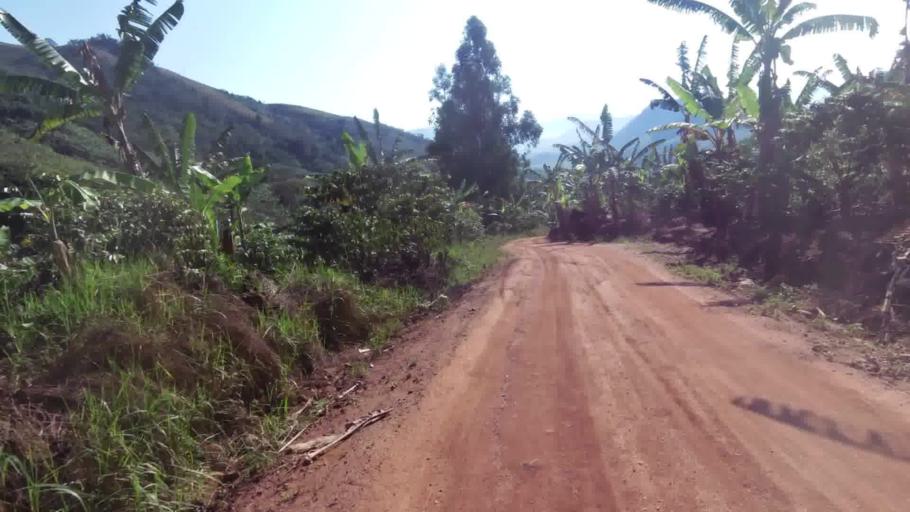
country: BR
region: Espirito Santo
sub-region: Alfredo Chaves
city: Alfredo Chaves
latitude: -20.6945
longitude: -40.7840
